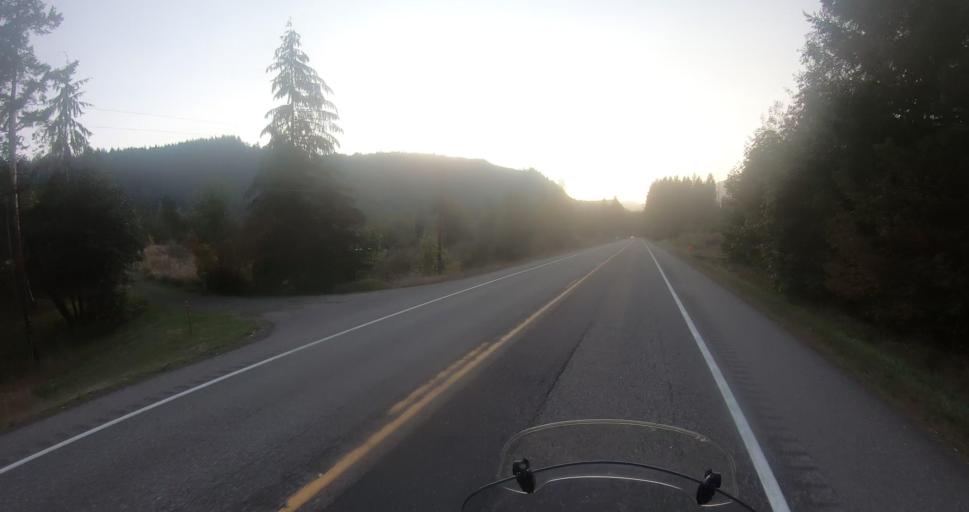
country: US
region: Washington
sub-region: Lewis County
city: Morton
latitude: 46.5393
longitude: -122.0329
